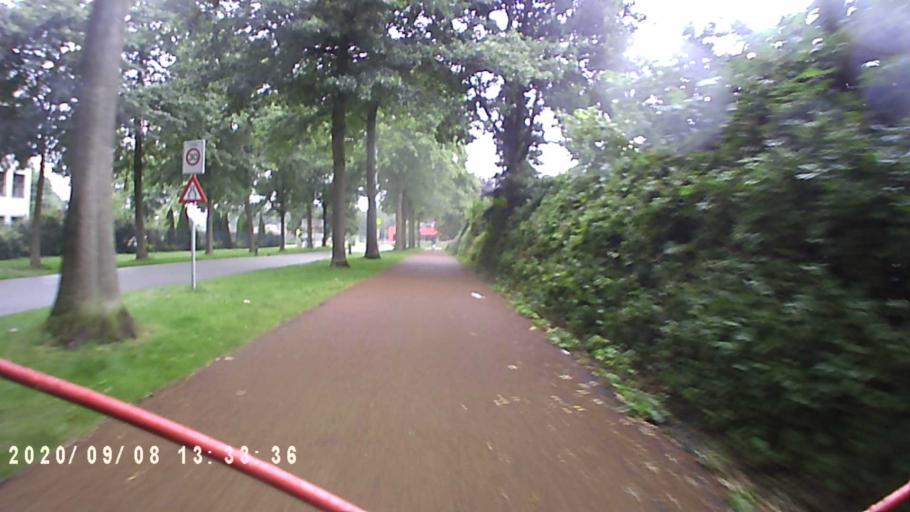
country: NL
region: Groningen
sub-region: Gemeente Veendam
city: Veendam
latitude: 53.1107
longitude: 6.8686
